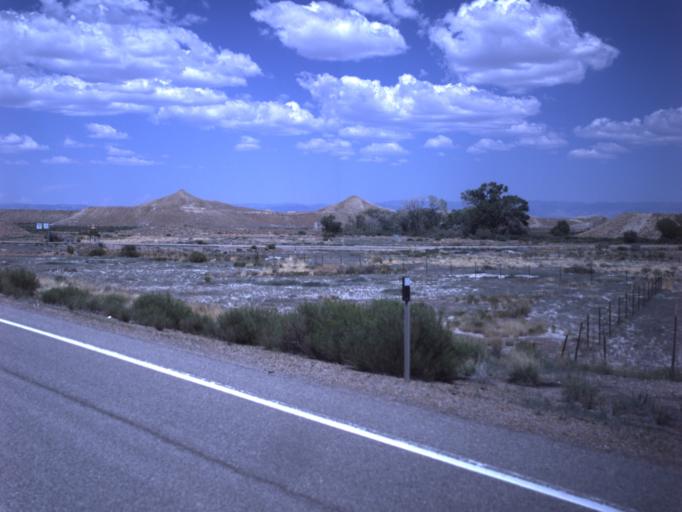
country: US
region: Utah
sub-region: Emery County
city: Huntington
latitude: 39.4318
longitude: -110.8680
